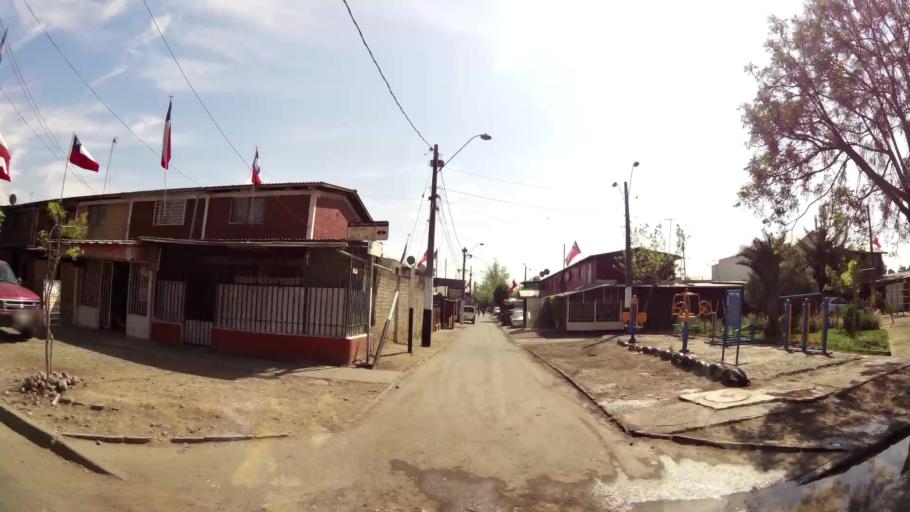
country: CL
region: Santiago Metropolitan
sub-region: Provincia de Santiago
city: La Pintana
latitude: -33.5573
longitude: -70.6506
